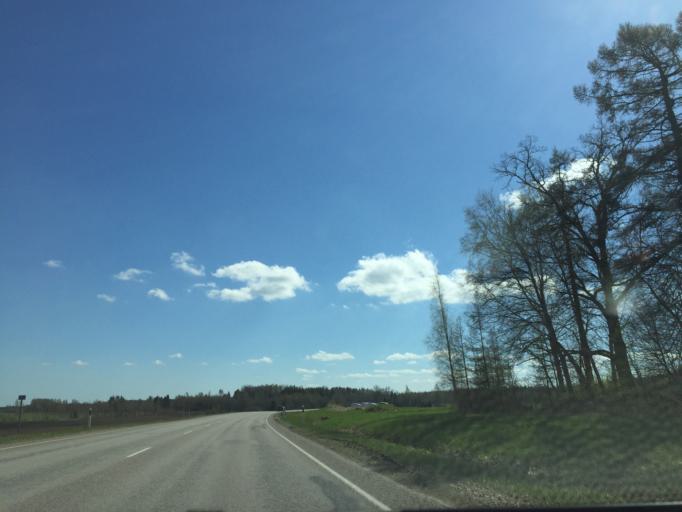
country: EE
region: Valgamaa
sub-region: Valga linn
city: Valga
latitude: 57.8760
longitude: 26.0603
